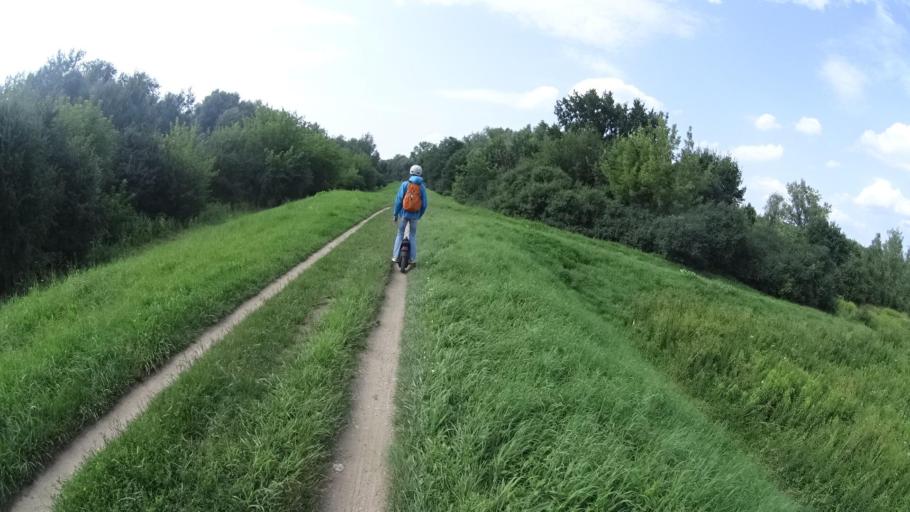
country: PL
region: Masovian Voivodeship
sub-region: Powiat legionowski
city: Jablonna
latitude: 52.3676
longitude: 20.9169
